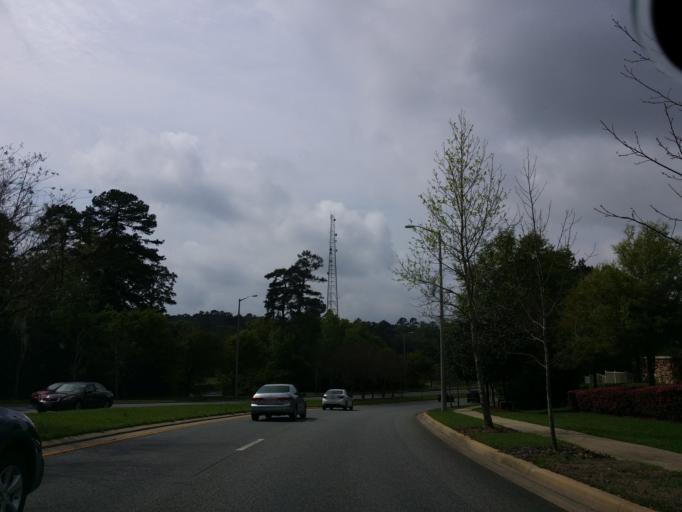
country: US
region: Florida
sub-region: Leon County
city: Tallahassee
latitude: 30.4592
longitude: -84.2434
